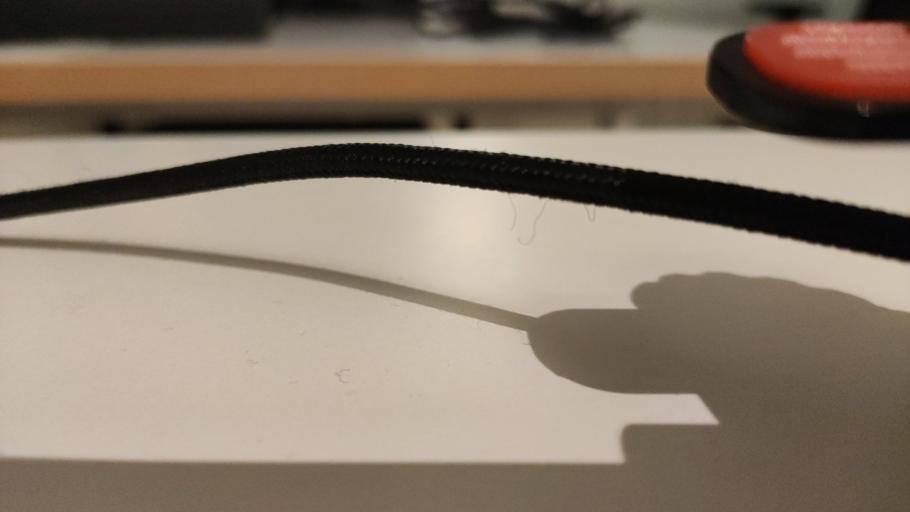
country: RU
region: Moskovskaya
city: Gorshkovo
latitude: 56.3737
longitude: 37.4141
